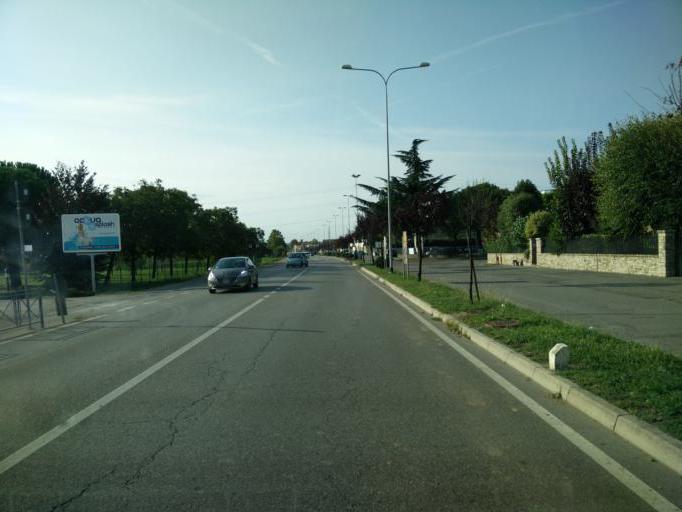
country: IT
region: Lombardy
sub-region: Provincia di Brescia
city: Colombaro-Timoline
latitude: 45.6324
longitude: 10.0087
